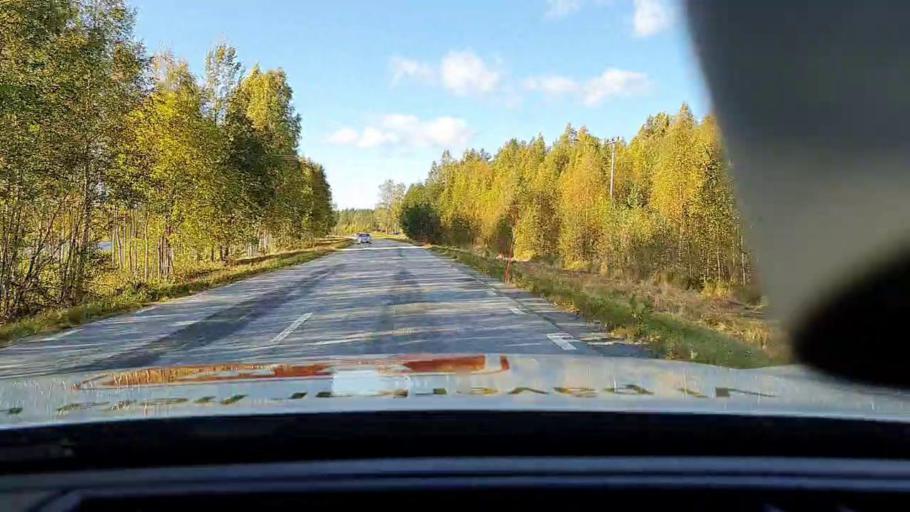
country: SE
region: Norrbotten
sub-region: Pitea Kommun
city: Norrfjarden
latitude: 65.4299
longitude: 21.4910
